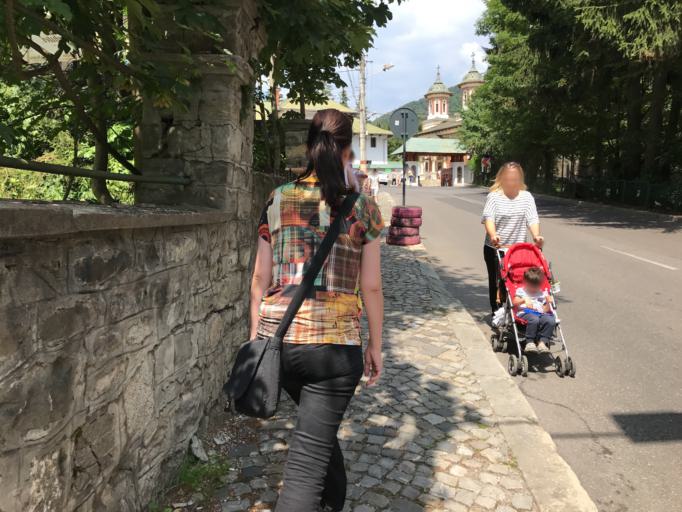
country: RO
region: Prahova
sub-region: Oras Sinaia
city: Sinaia
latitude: 45.3546
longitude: 25.5487
